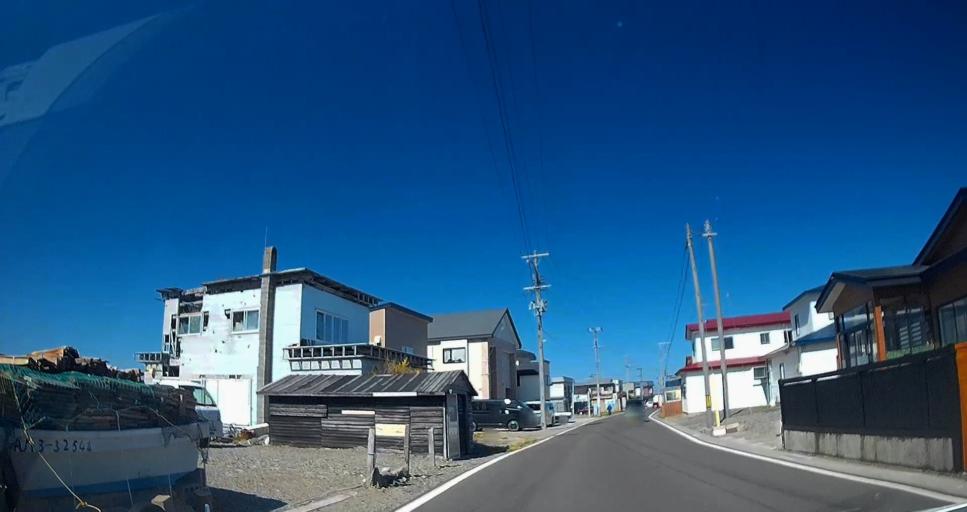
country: JP
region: Hokkaido
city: Hakodate
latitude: 41.5271
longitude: 140.9039
